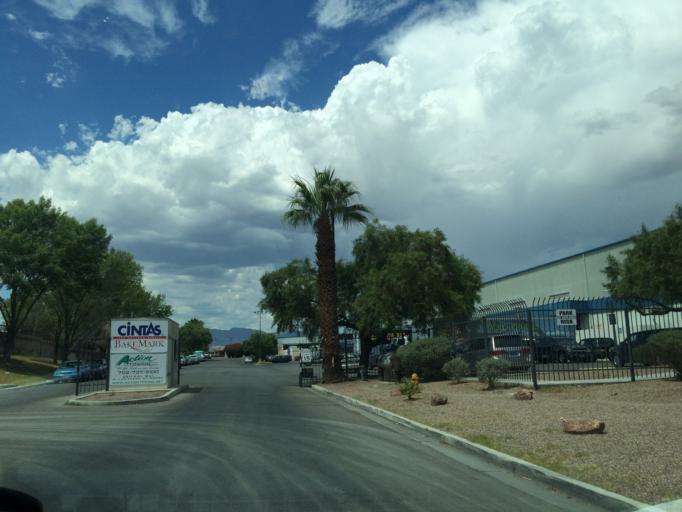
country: US
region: Nevada
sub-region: Clark County
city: North Las Vegas
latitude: 36.2034
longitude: -115.1401
